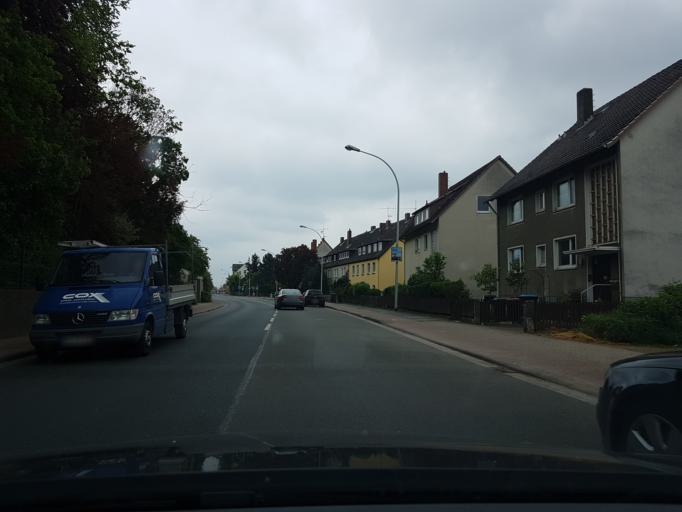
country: DE
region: Lower Saxony
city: Hameln
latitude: 52.1085
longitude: 9.3722
